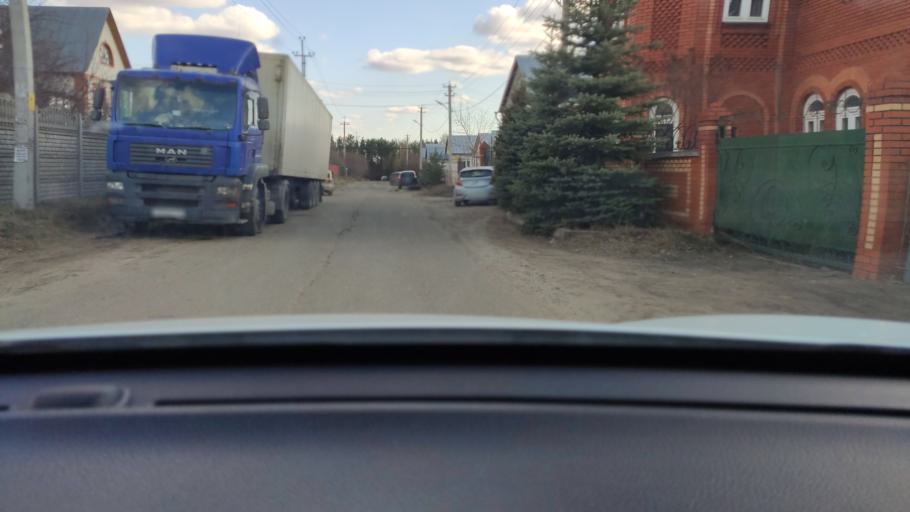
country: RU
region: Tatarstan
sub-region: Gorod Kazan'
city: Kazan
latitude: 55.8100
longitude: 49.2190
